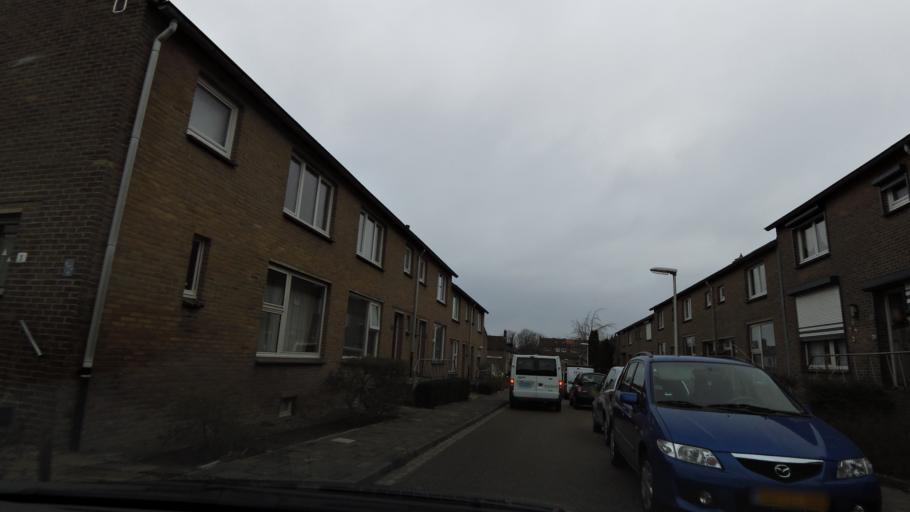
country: NL
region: Limburg
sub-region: Gemeente Heerlen
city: Heerlen
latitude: 50.8992
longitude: 5.9915
